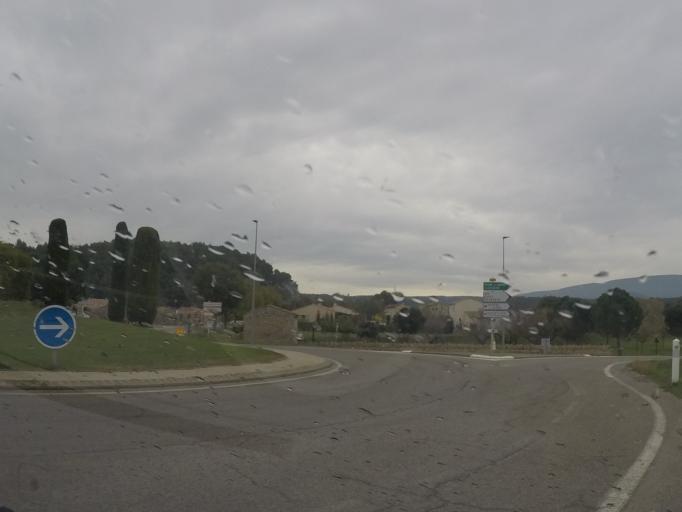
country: FR
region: Provence-Alpes-Cote d'Azur
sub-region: Departement du Vaucluse
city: Menerbes
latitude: 43.8598
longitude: 5.1968
